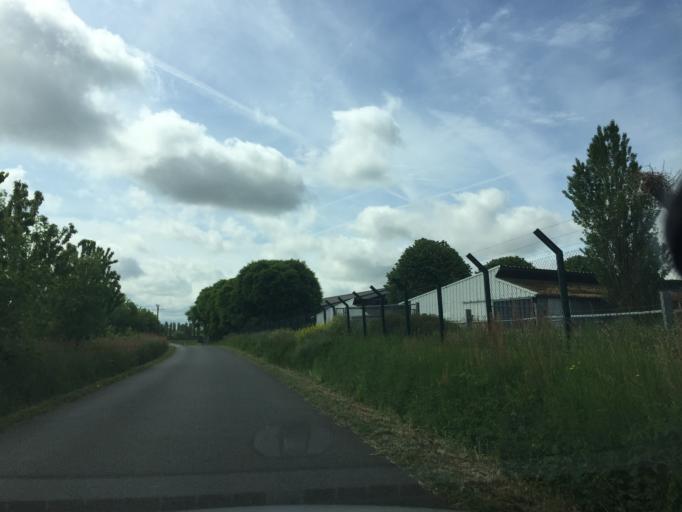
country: FR
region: Brittany
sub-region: Departement des Cotes-d'Armor
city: Crehen
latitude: 48.5502
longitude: -2.1917
